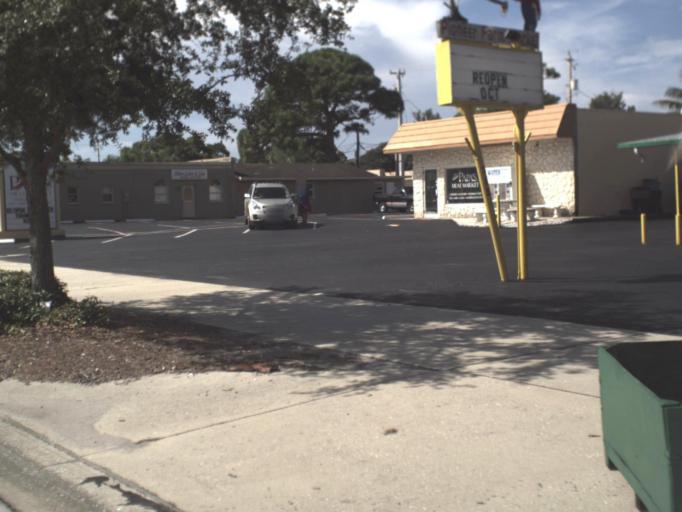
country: US
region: Florida
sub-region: Sarasota County
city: Venice
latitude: 27.0955
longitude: -82.4444
